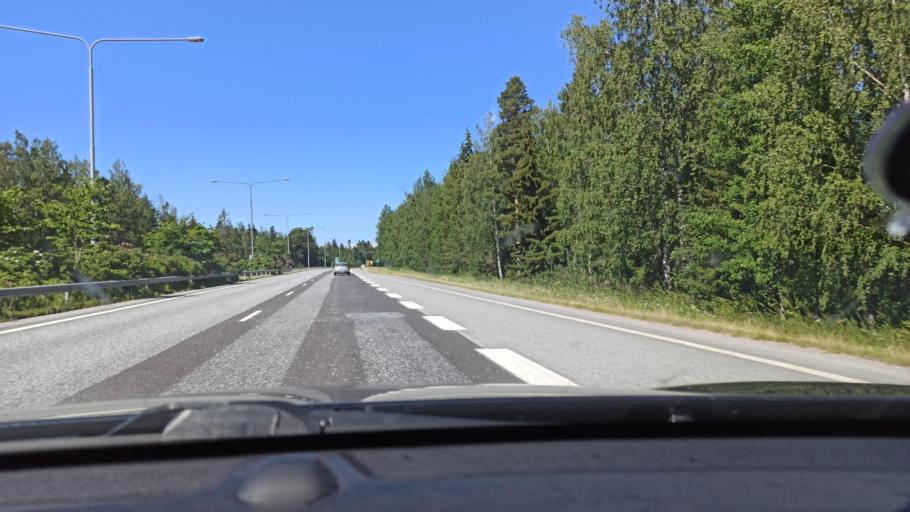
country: FI
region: Ostrobothnia
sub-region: Vaasa
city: Vaasa
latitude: 63.0810
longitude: 21.6427
